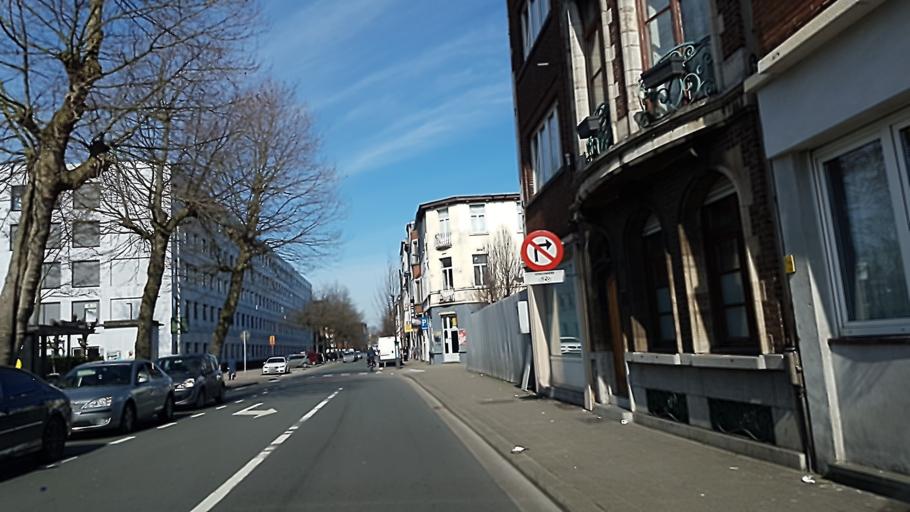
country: BE
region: Flanders
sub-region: Provincie Antwerpen
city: Antwerpen
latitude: 51.2228
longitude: 4.4369
